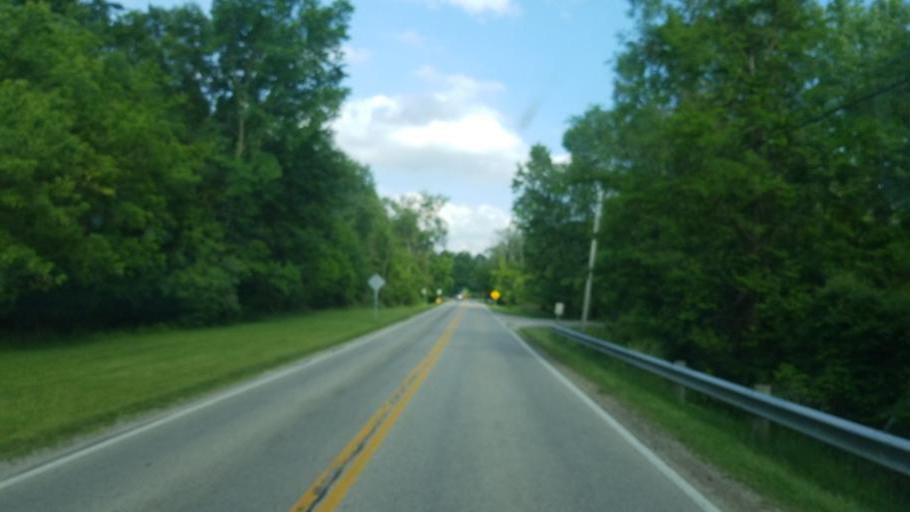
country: US
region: Ohio
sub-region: Franklin County
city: Westerville
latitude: 40.1718
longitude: -82.8826
